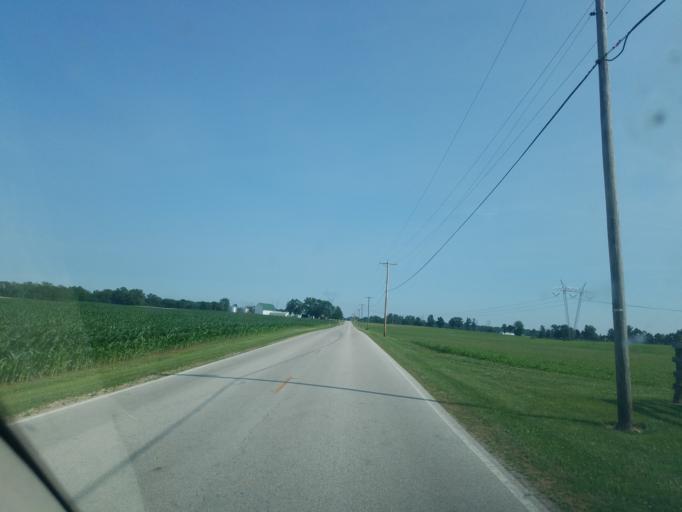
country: US
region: Ohio
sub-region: Wyandot County
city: Upper Sandusky
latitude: 40.9625
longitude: -83.2291
